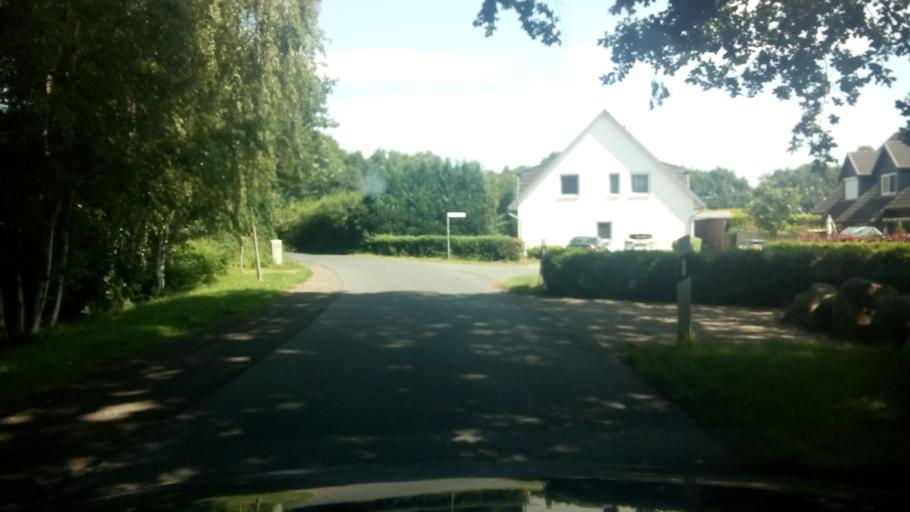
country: DE
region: Lower Saxony
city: Osterholz-Scharmbeck
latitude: 53.2518
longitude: 8.8199
